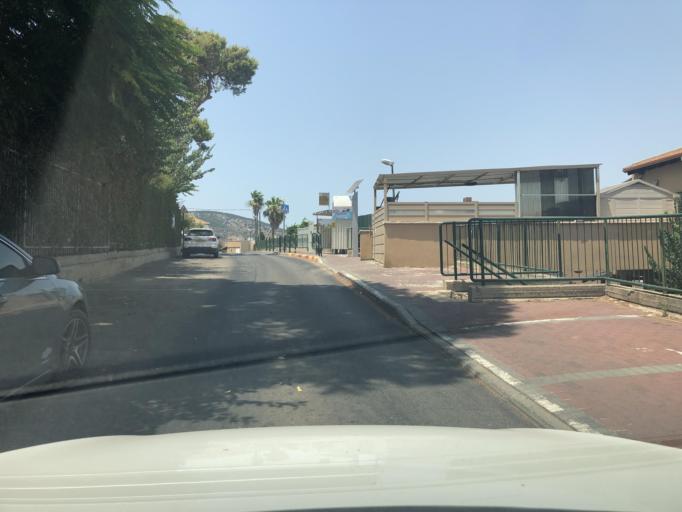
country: IL
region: Haifa
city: Daliyat el Karmil
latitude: 32.6592
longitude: 35.1113
